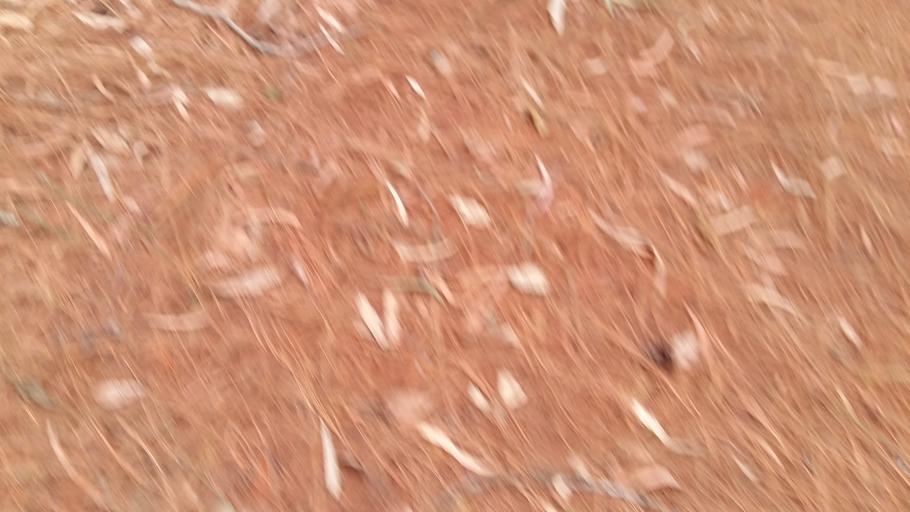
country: GT
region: Guatemala
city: Santa Catarina Pinula
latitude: 14.5992
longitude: -90.4851
